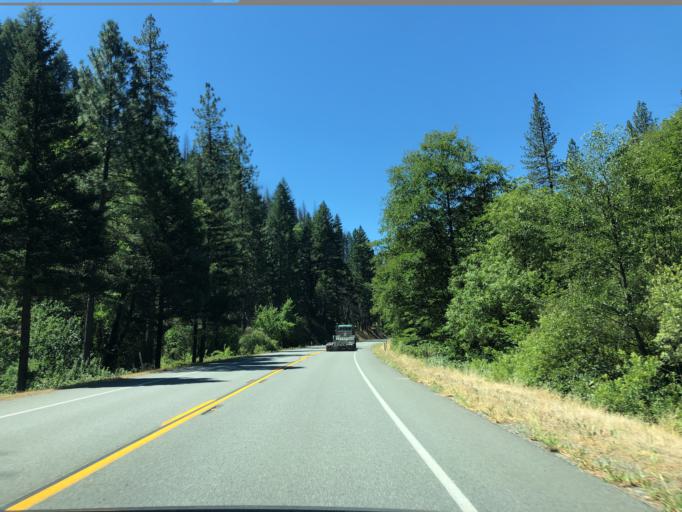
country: US
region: California
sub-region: Trinity County
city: Weaverville
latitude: 40.7019
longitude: -122.9256
